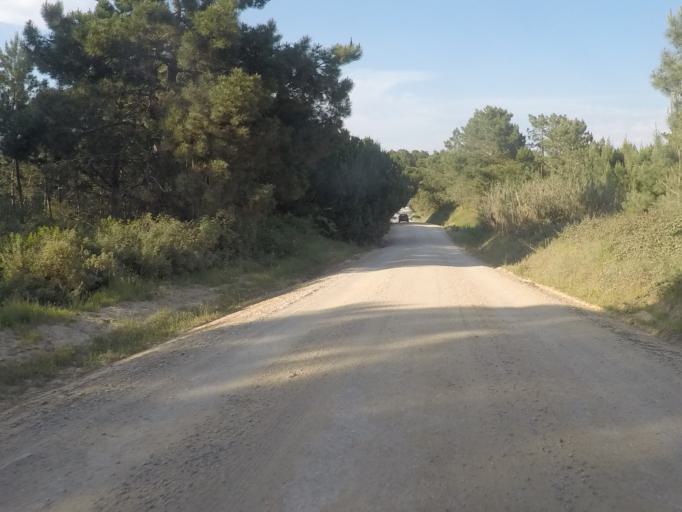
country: PT
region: Setubal
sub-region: Sesimbra
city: Sesimbra
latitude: 38.4559
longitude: -9.1893
